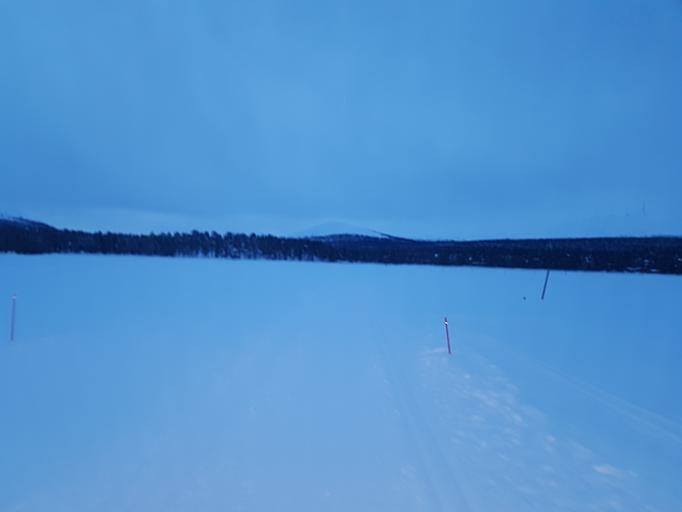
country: FI
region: Lapland
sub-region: Tunturi-Lappi
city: Kolari
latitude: 67.6100
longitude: 24.1642
